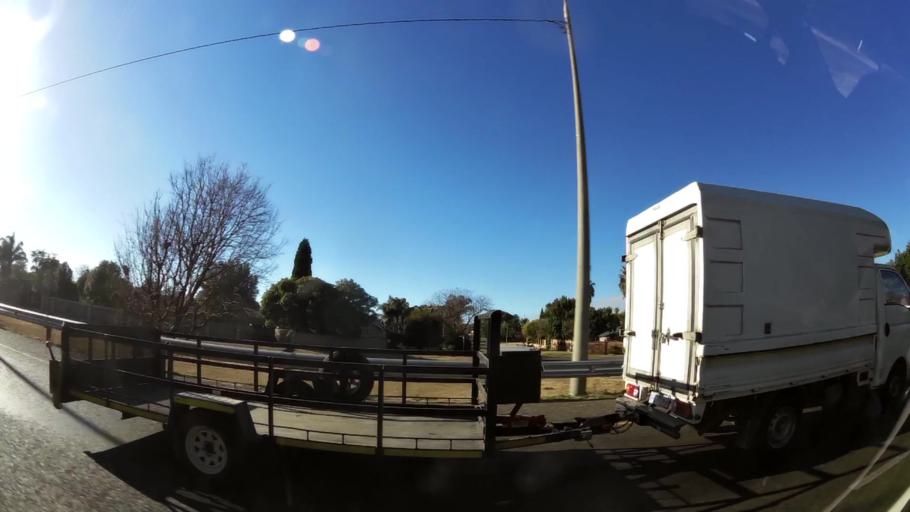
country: ZA
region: Gauteng
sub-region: West Rand District Municipality
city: Krugersdorp
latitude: -26.0852
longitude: 27.7881
